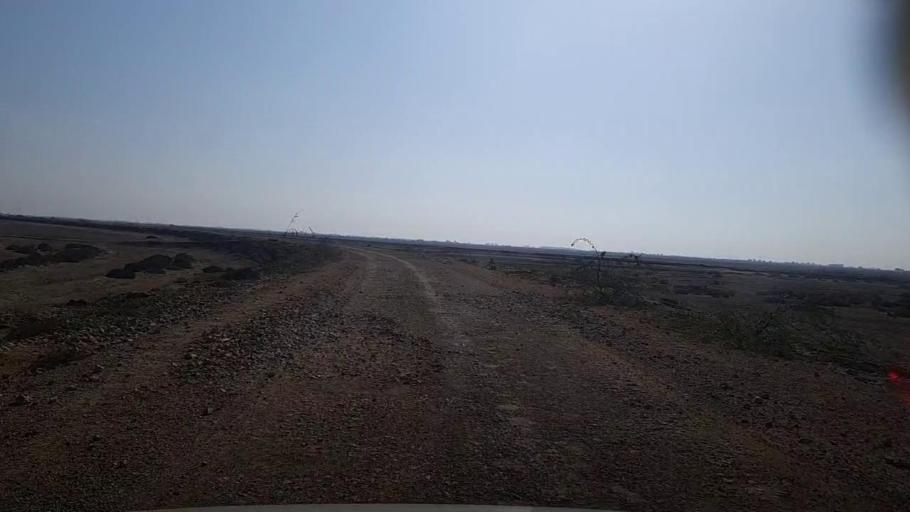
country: PK
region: Sindh
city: Mirpur Sakro
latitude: 24.5173
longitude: 67.4936
